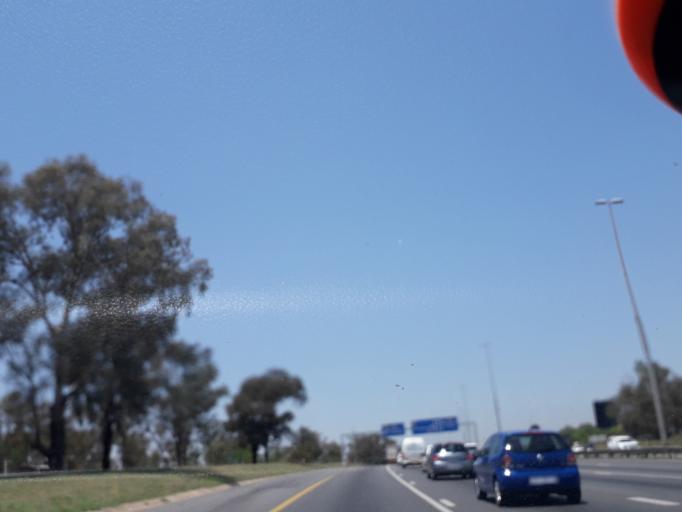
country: ZA
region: Gauteng
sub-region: City of Johannesburg Metropolitan Municipality
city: Midrand
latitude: -26.0421
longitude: 28.0854
